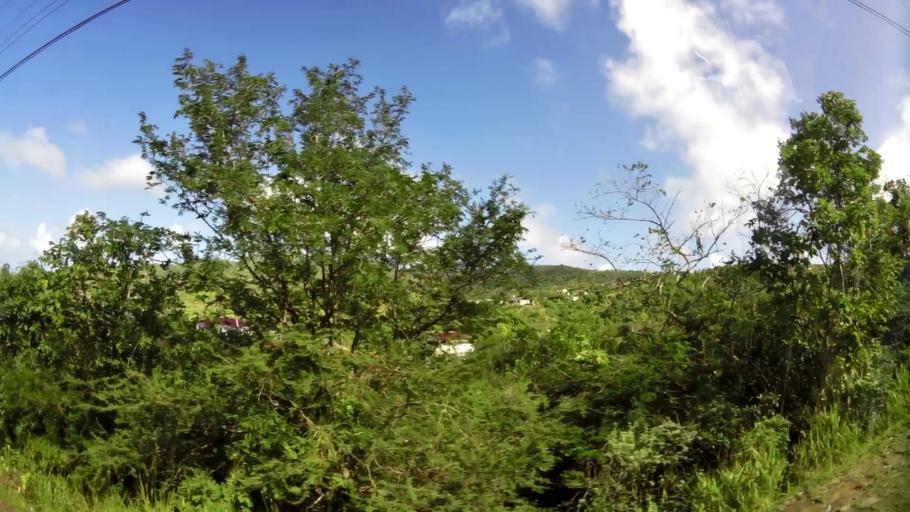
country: MS
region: Saint Peter
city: Brades
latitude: 16.7931
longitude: -62.2102
